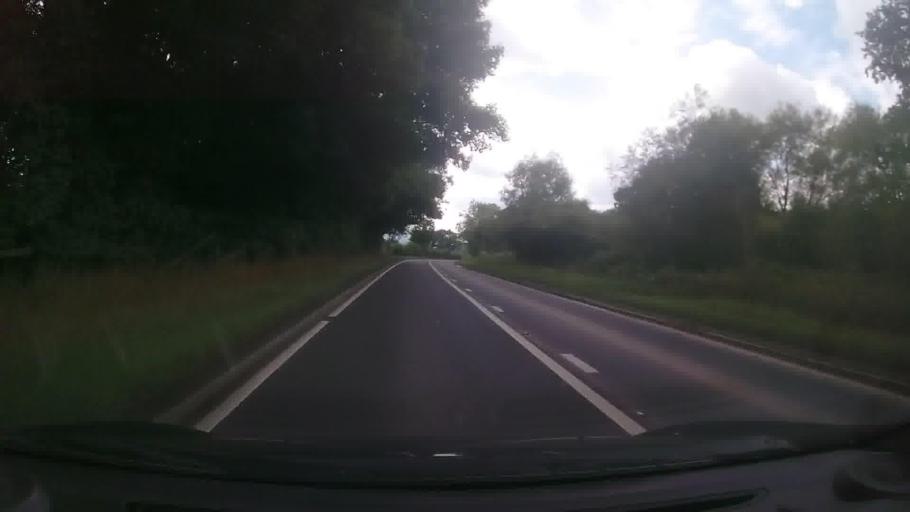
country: GB
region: Wales
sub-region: Sir Powys
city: Welshpool
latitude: 52.7099
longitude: -3.0958
